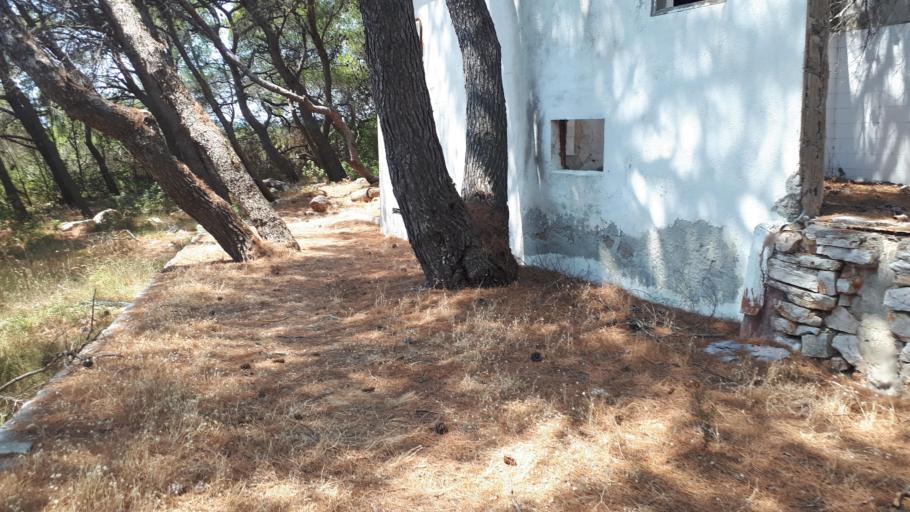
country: HR
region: Splitsko-Dalmatinska
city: Jelsa
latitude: 43.1903
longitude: 16.6930
